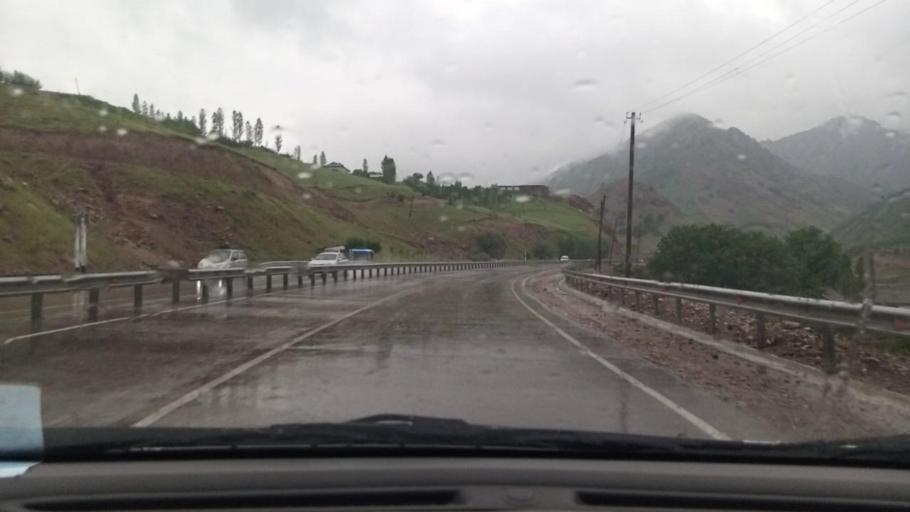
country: UZ
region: Toshkent
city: Angren
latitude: 41.0992
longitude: 70.3238
